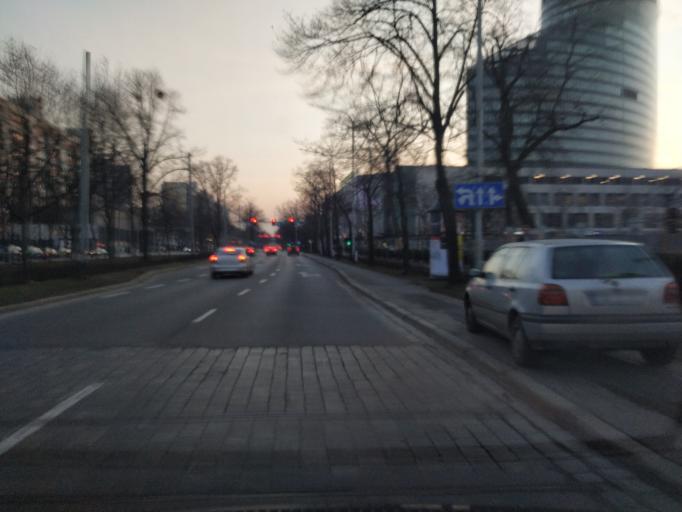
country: PL
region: Lower Silesian Voivodeship
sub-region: Powiat wroclawski
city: Wroclaw
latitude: 51.0956
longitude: 17.0226
